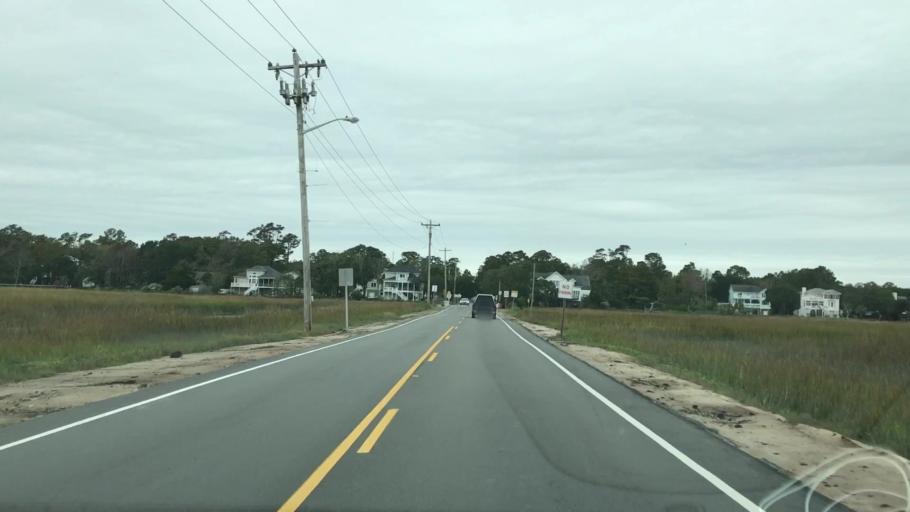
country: US
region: South Carolina
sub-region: Horry County
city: Garden City
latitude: 33.5826
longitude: -78.9971
